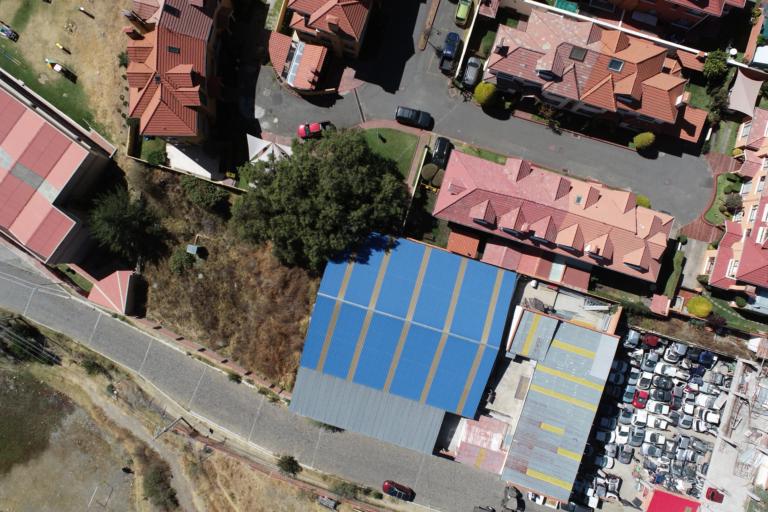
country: BO
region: La Paz
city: La Paz
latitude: -16.5389
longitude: -68.0593
